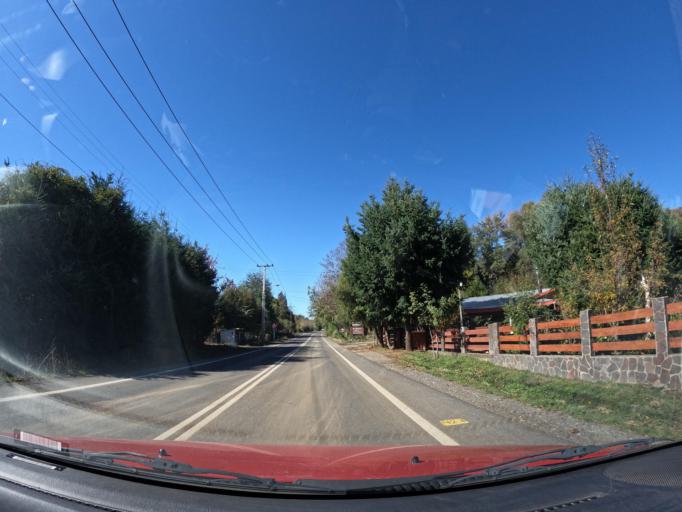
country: CL
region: Biobio
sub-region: Provincia de Nuble
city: Coihueco
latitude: -36.8163
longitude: -71.7216
